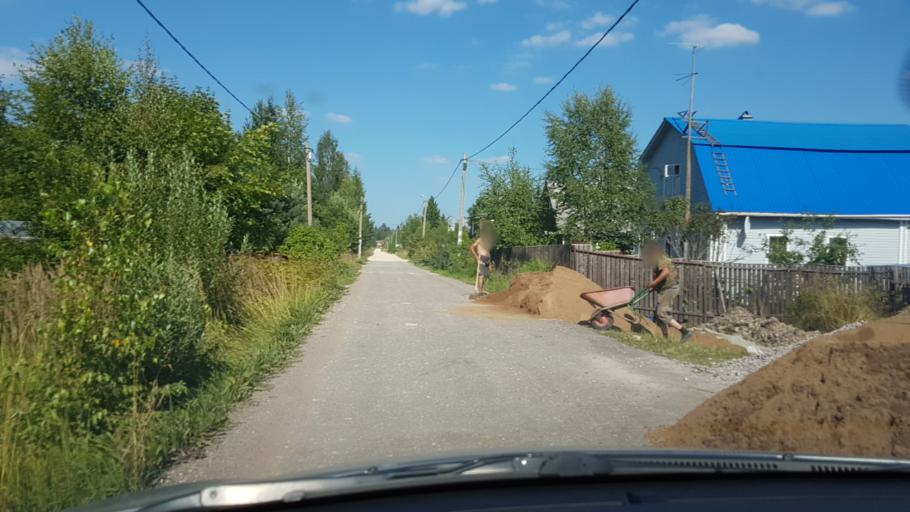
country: RU
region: Leningrad
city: Vyritsa
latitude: 59.4501
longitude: 30.2965
